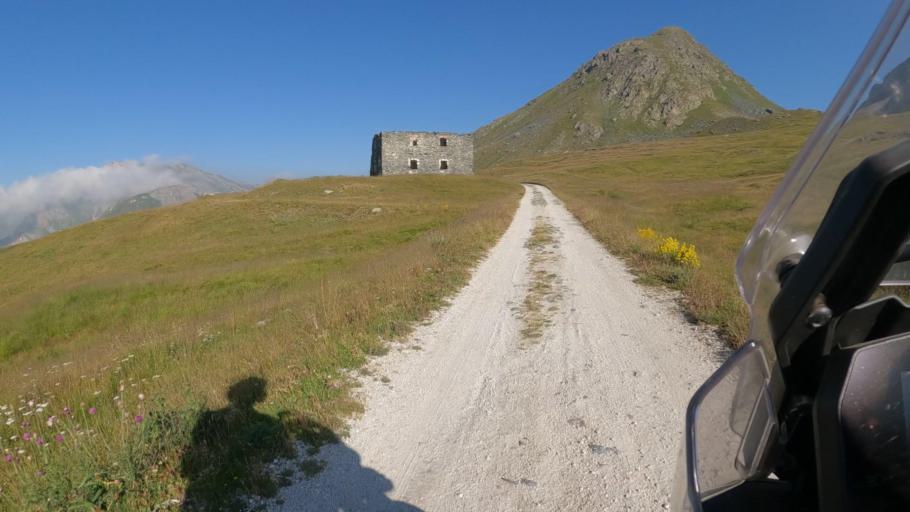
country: IT
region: Piedmont
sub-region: Provincia di Cuneo
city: Sambuco
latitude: 44.3824
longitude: 7.0842
